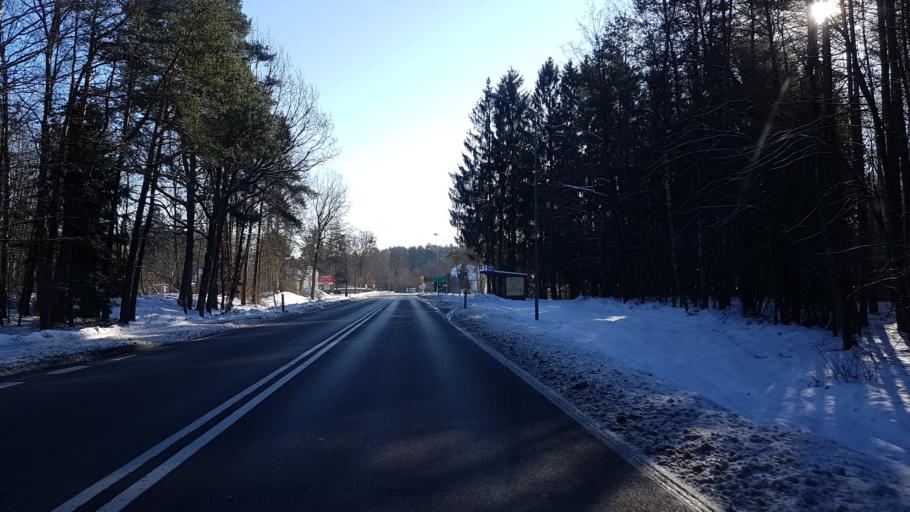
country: PL
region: West Pomeranian Voivodeship
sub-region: Powiat koszalinski
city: Sianow
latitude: 54.0774
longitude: 16.3933
